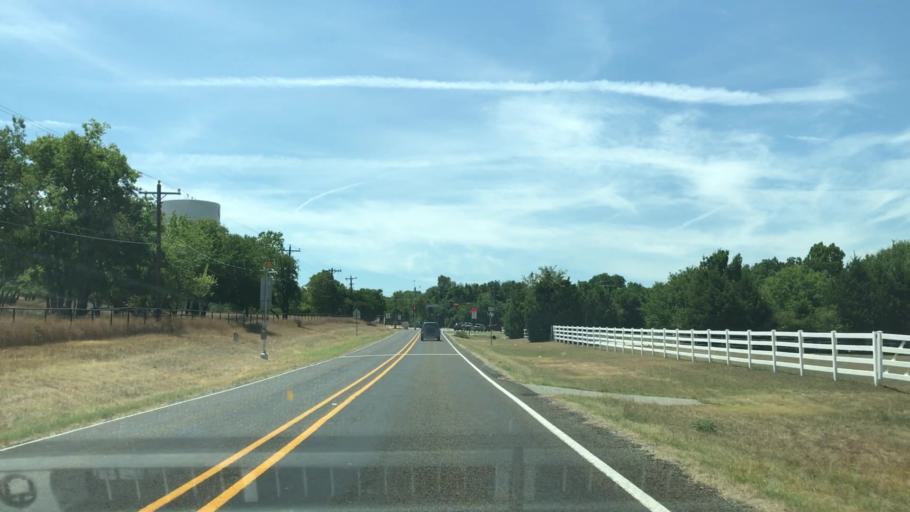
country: US
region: Texas
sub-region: Collin County
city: Fairview
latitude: 33.1335
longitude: -96.6095
